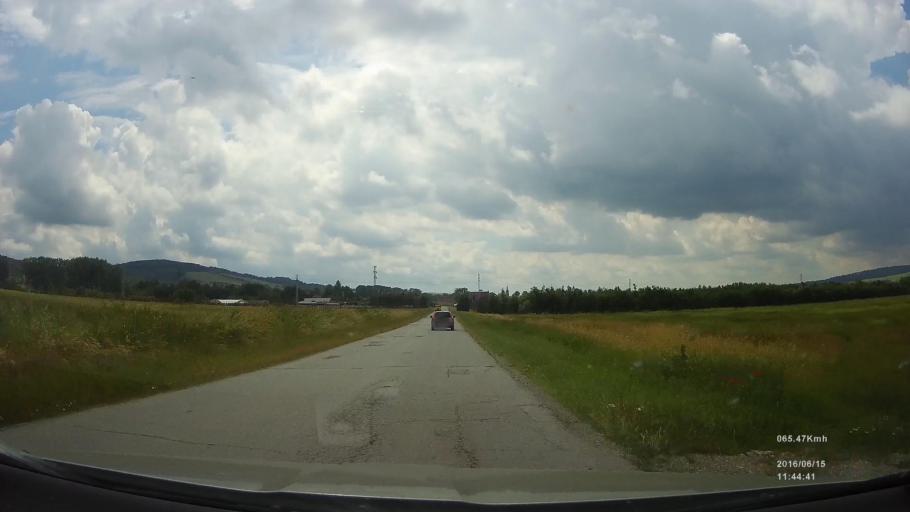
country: SK
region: Kosicky
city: Kosice
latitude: 48.7421
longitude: 21.3455
